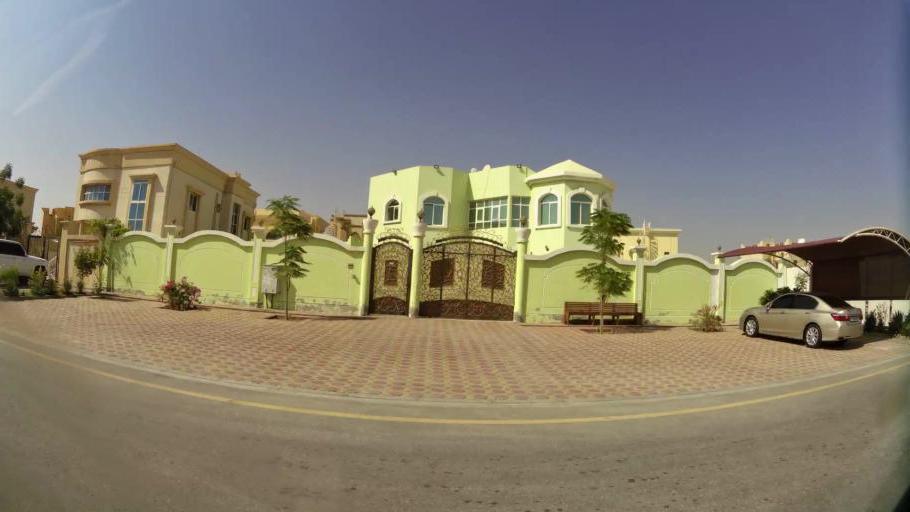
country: AE
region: Ajman
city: Ajman
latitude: 25.4144
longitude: 55.5382
